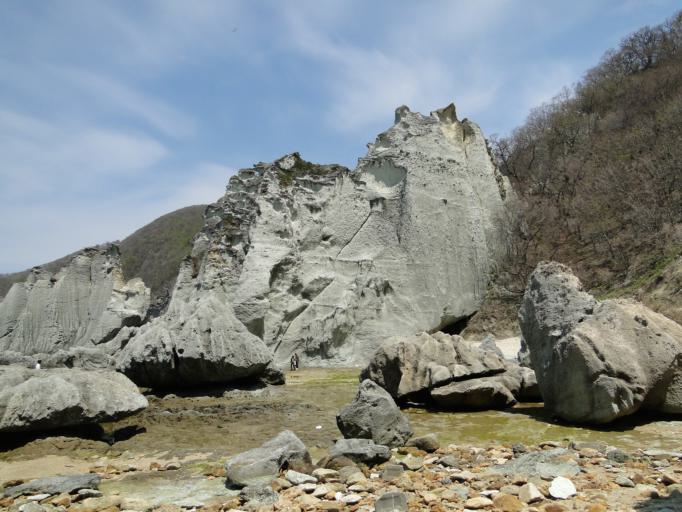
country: JP
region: Aomori
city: Mutsu
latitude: 41.3089
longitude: 140.8039
